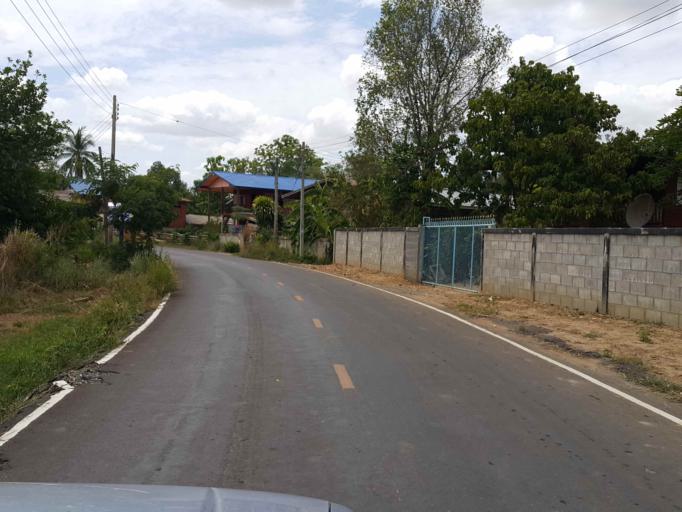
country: TH
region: Sukhothai
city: Thung Saliam
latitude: 17.3269
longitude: 99.5588
